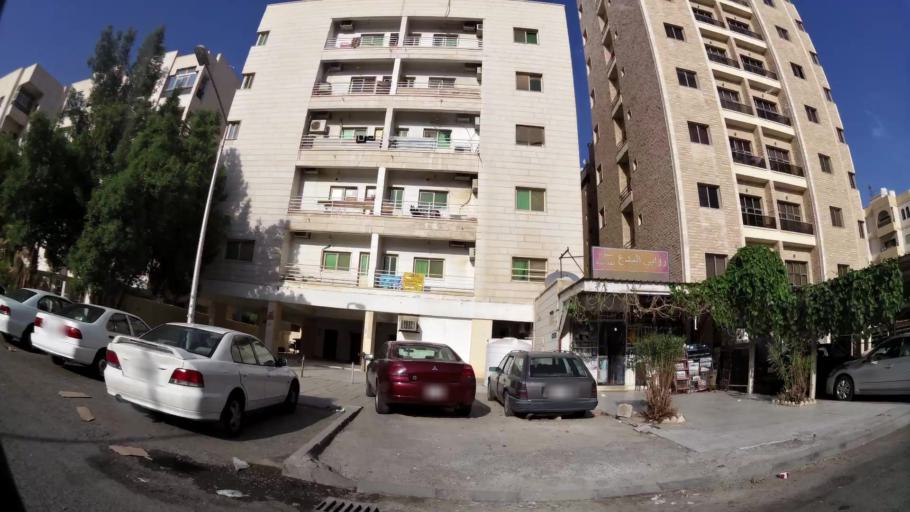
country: KW
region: Muhafazat Hawalli
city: As Salimiyah
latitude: 29.3357
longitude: 48.0838
